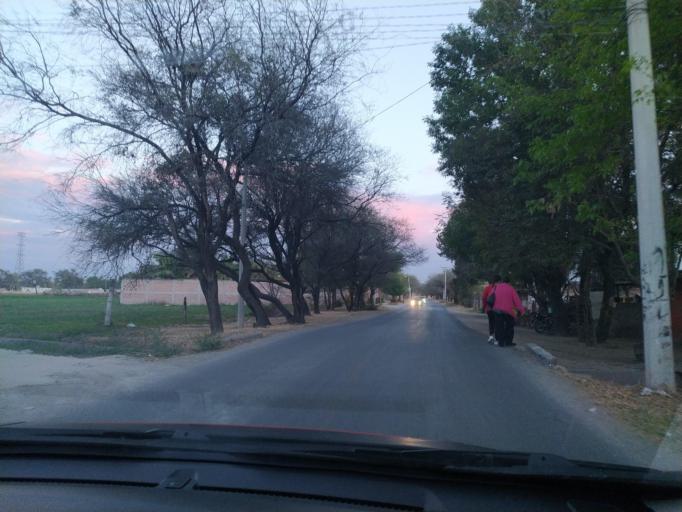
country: MX
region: Guanajuato
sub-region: San Francisco del Rincon
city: San Roque de Montes
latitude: 21.0186
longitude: -101.8227
